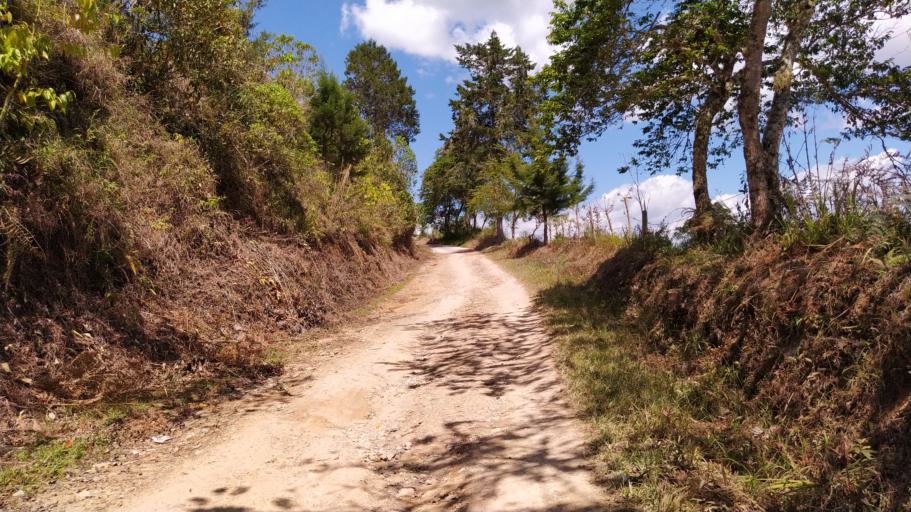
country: CO
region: Valle del Cauca
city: El Cairo
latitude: 4.7554
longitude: -76.2268
